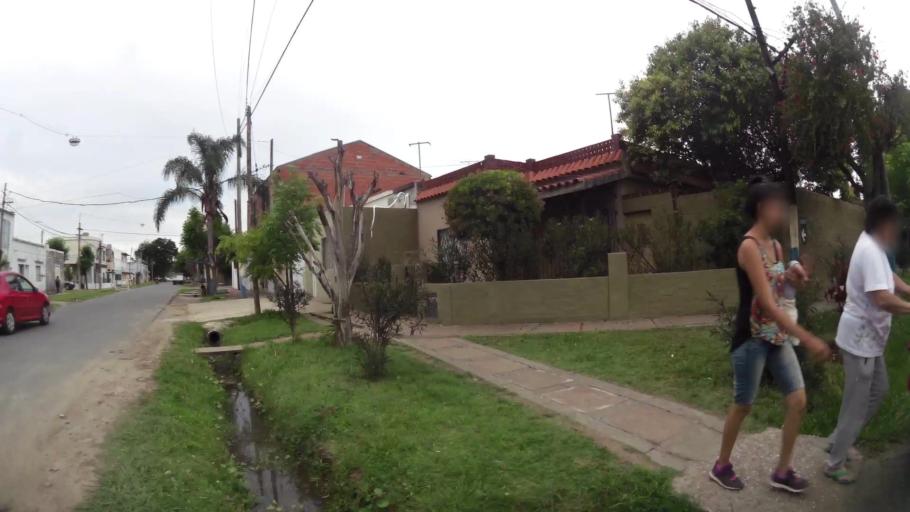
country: AR
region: Santa Fe
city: Granadero Baigorria
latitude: -32.8966
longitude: -60.7029
